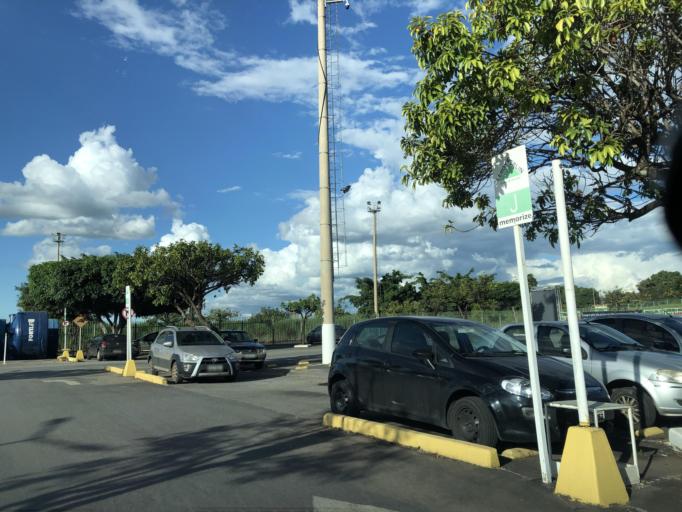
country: BR
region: Federal District
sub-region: Brasilia
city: Brasilia
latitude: -15.7529
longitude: -47.9273
